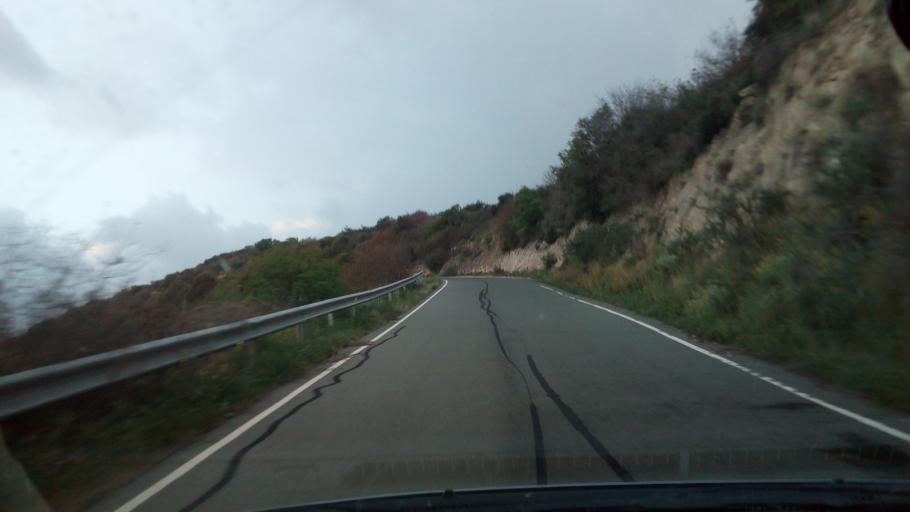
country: CY
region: Pafos
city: Polis
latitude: 34.9657
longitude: 32.4424
